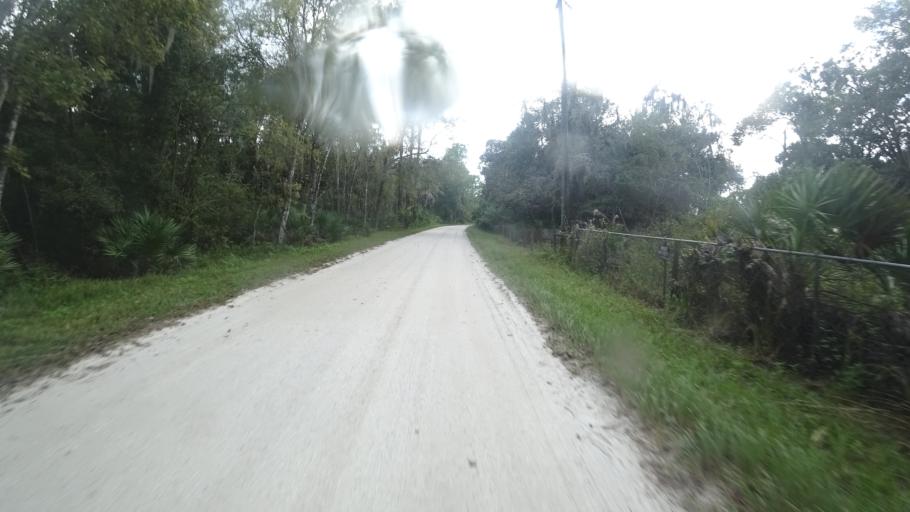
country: US
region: Florida
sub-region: Hillsborough County
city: Wimauma
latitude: 27.6056
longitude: -82.2109
